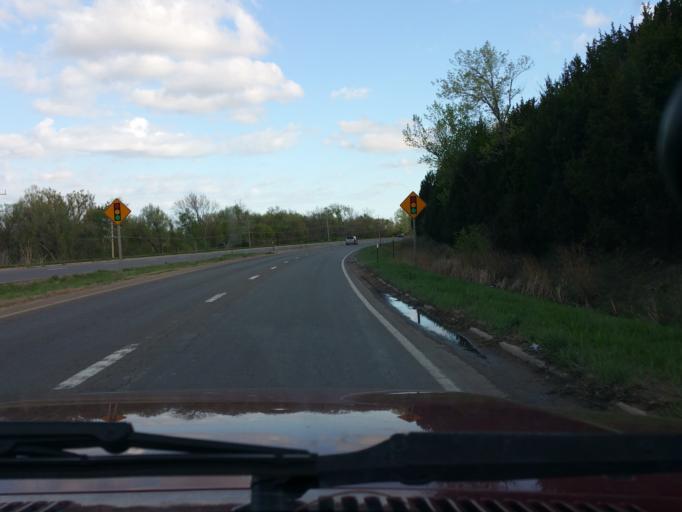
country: US
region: Kansas
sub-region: Riley County
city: Manhattan
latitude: 39.2006
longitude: -96.5643
